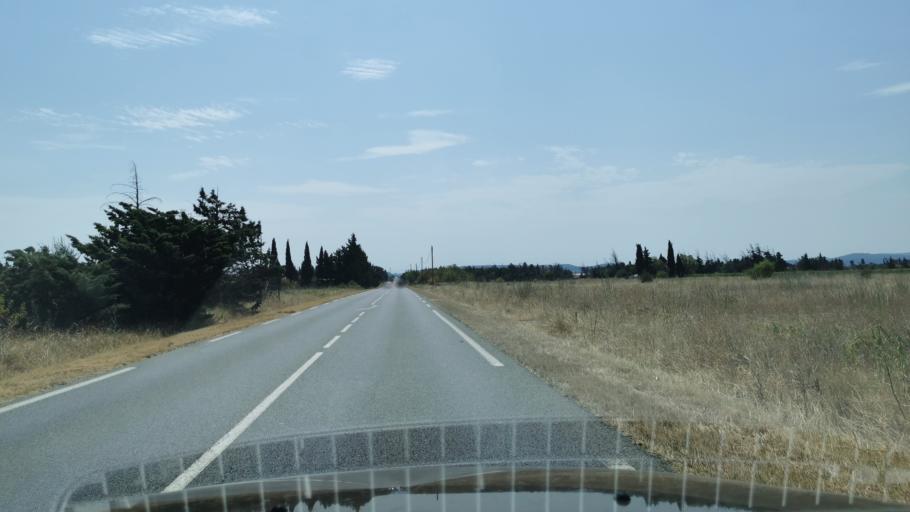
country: FR
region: Languedoc-Roussillon
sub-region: Departement de l'Aude
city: Ginestas
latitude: 43.2687
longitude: 2.8958
